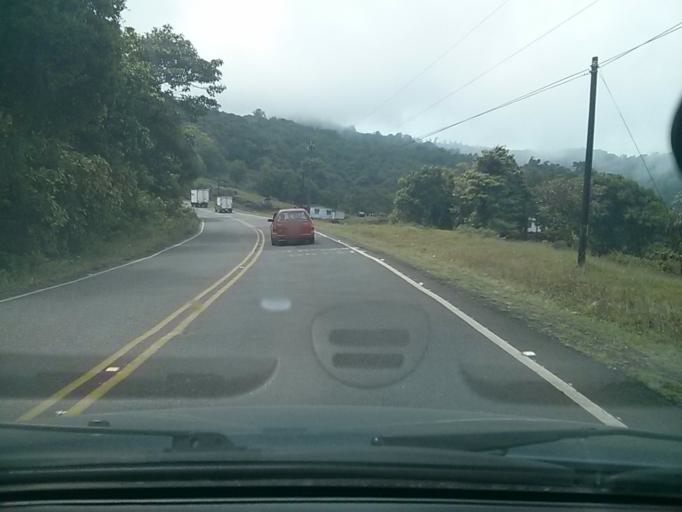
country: CR
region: San Jose
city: San Marcos
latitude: 9.7413
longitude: -83.9641
